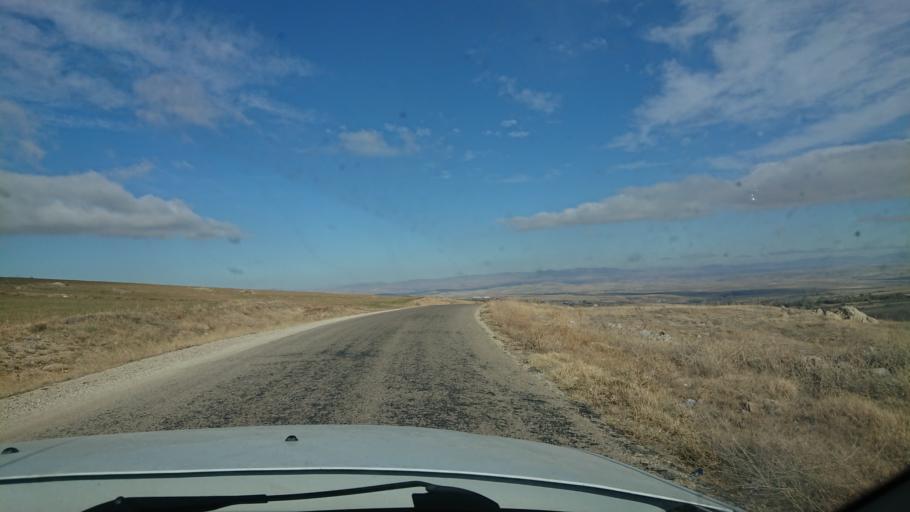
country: TR
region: Aksaray
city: Agacoren
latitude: 38.8403
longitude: 33.9526
